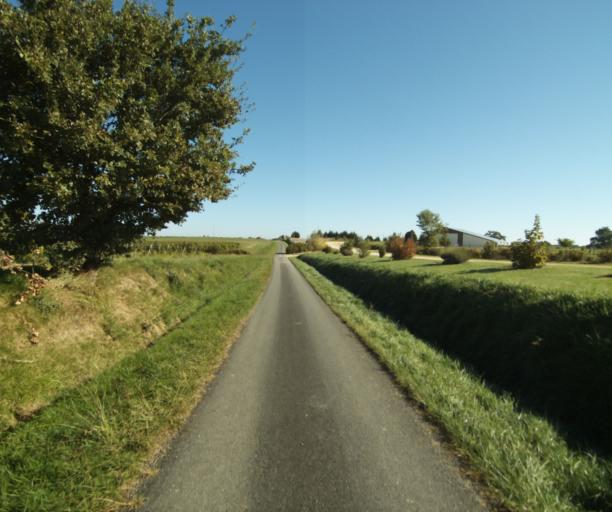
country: FR
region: Midi-Pyrenees
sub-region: Departement du Gers
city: Gondrin
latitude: 43.8145
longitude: 0.2064
